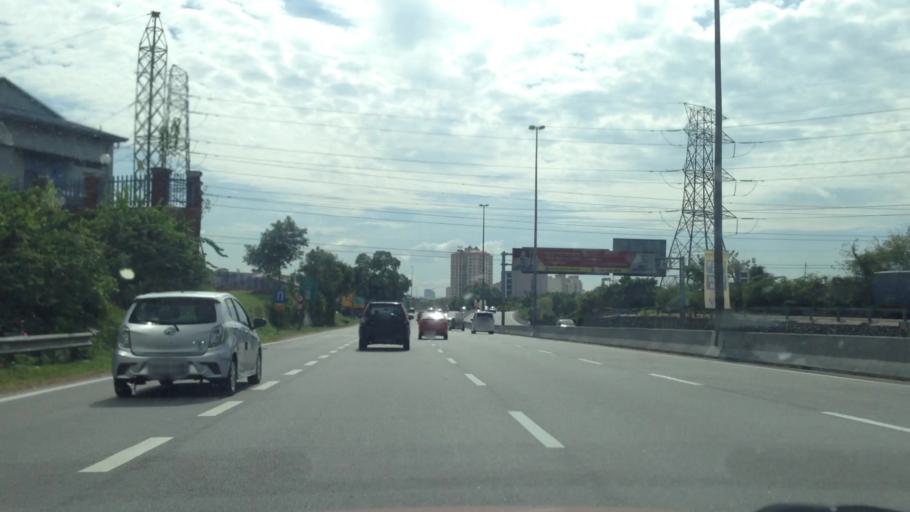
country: MY
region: Selangor
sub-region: Petaling
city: Petaling Jaya
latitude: 3.0757
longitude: 101.6189
